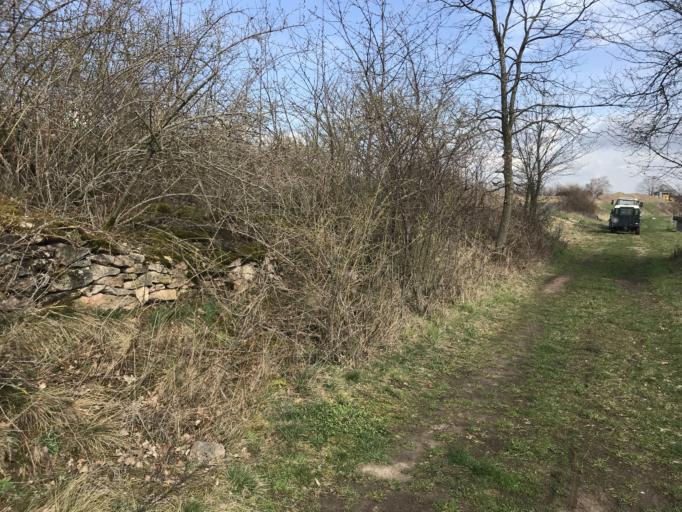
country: DE
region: Rheinland-Pfalz
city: Siefersheim
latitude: 49.7904
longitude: 7.9402
